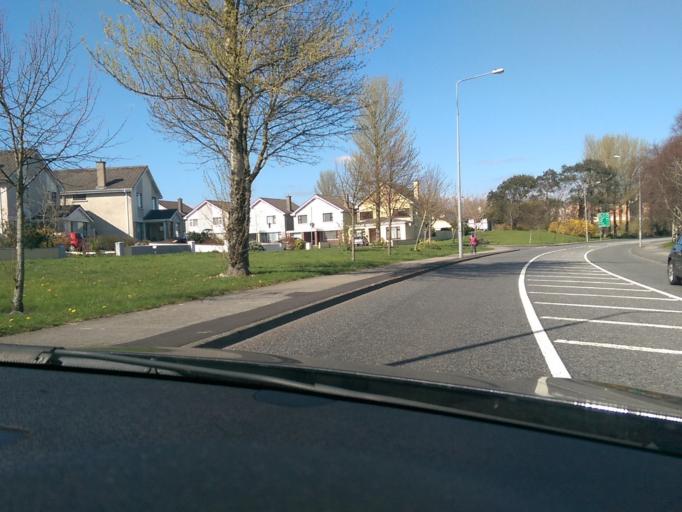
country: IE
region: Connaught
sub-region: County Galway
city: Gaillimh
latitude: 53.2867
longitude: -9.0749
